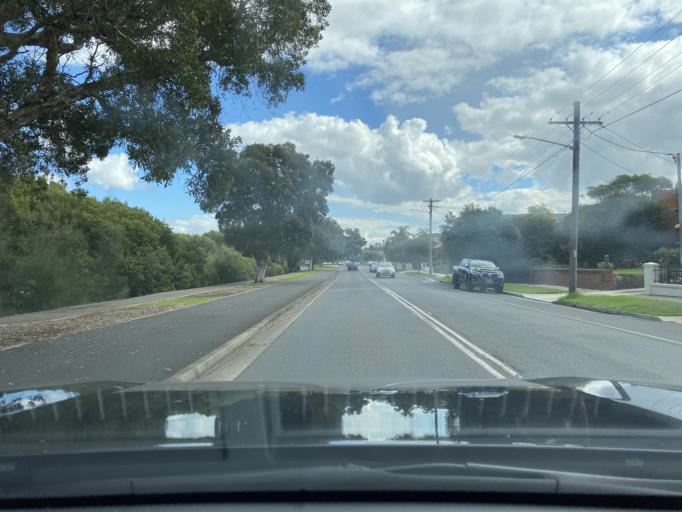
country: AU
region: New South Wales
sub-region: Leichhardt
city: Leichhardt
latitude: -33.8676
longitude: 151.1439
